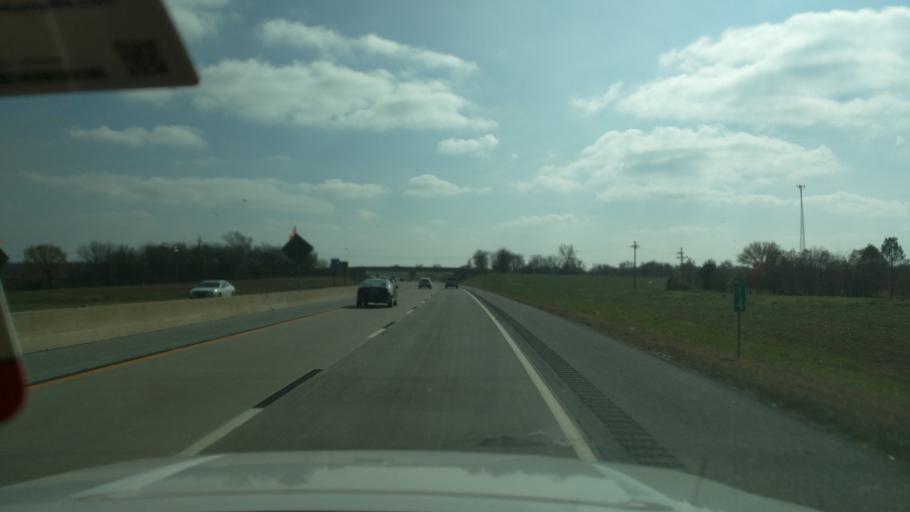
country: US
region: Oklahoma
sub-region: Wagoner County
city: Coweta
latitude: 35.9339
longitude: -95.5835
